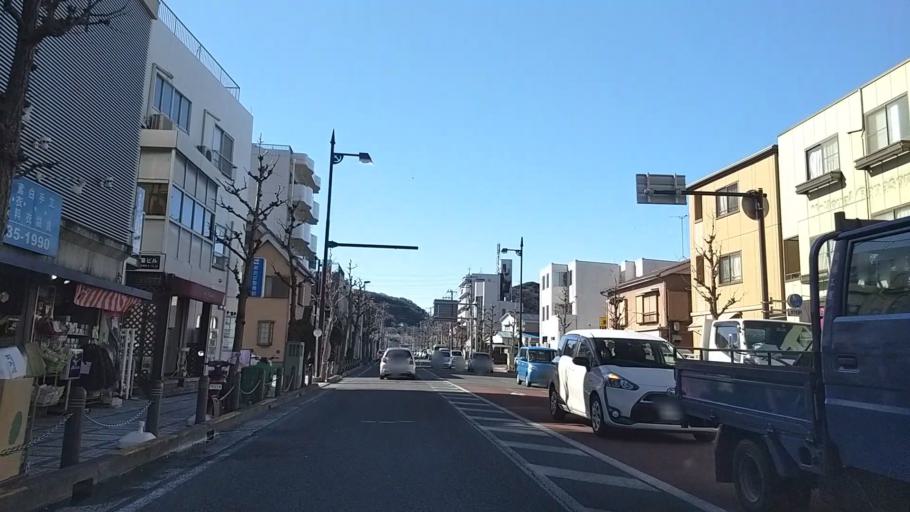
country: JP
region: Kanagawa
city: Yokosuka
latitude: 35.2290
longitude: 139.7030
